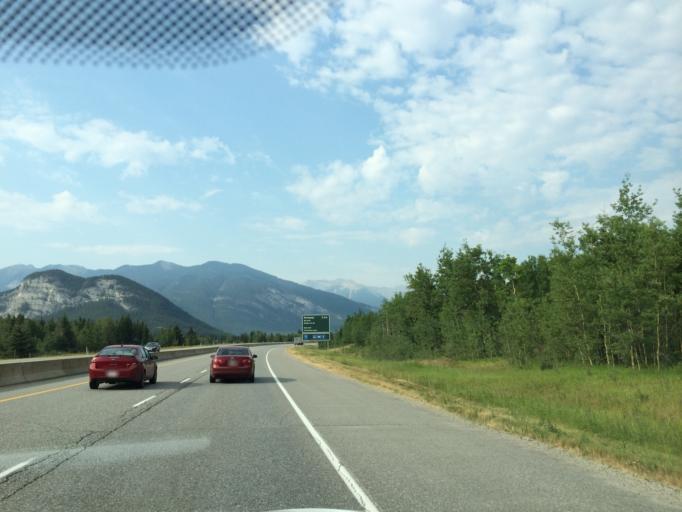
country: CA
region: Alberta
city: Banff
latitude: 51.2000
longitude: -115.5457
